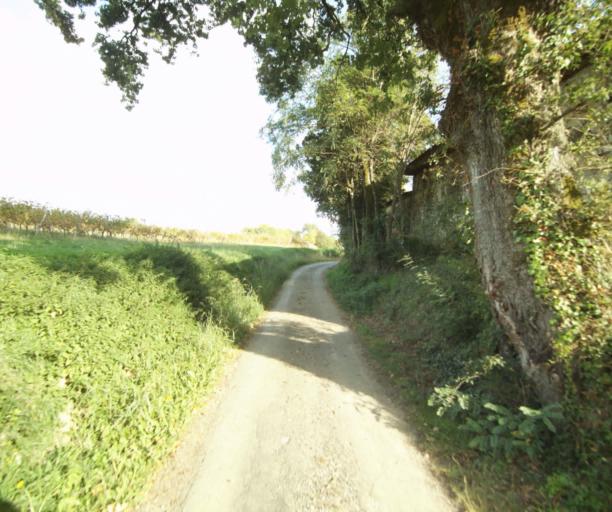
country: FR
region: Midi-Pyrenees
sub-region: Departement du Gers
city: Gondrin
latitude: 43.8880
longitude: 0.2342
